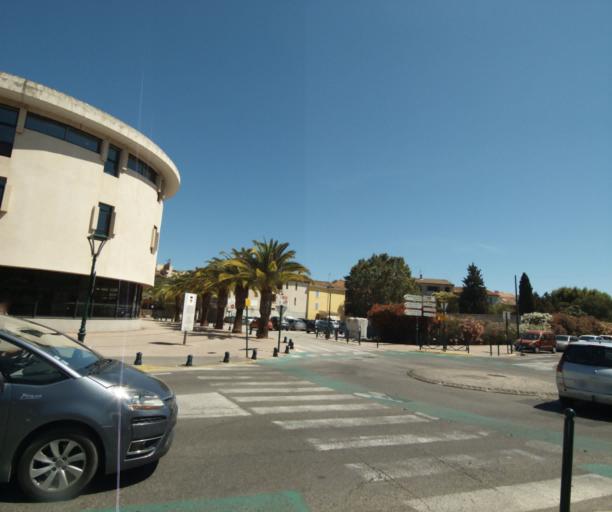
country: FR
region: Provence-Alpes-Cote d'Azur
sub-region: Departement du Var
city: La Garde
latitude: 43.1263
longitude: 6.0094
